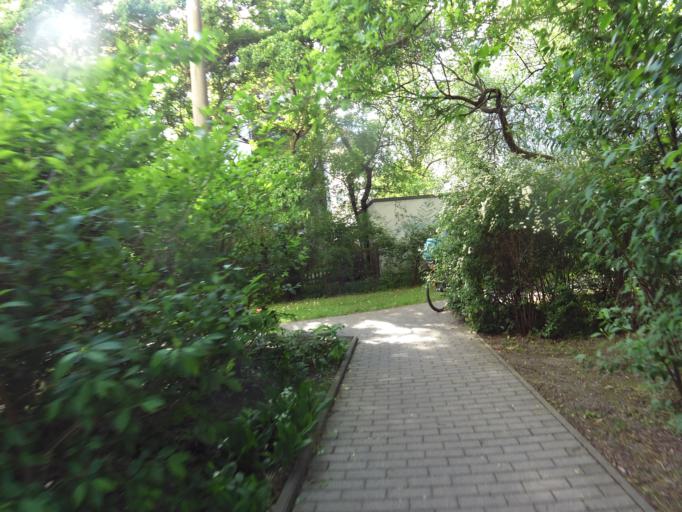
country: DE
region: Saxony
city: Leipzig
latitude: 51.3186
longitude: 12.4161
